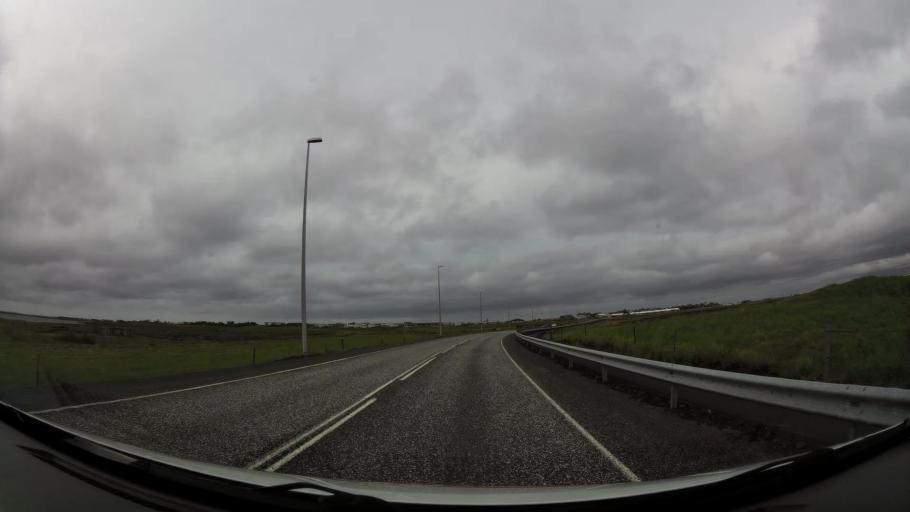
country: IS
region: Capital Region
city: Alftanes
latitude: 64.0972
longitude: -22.0038
